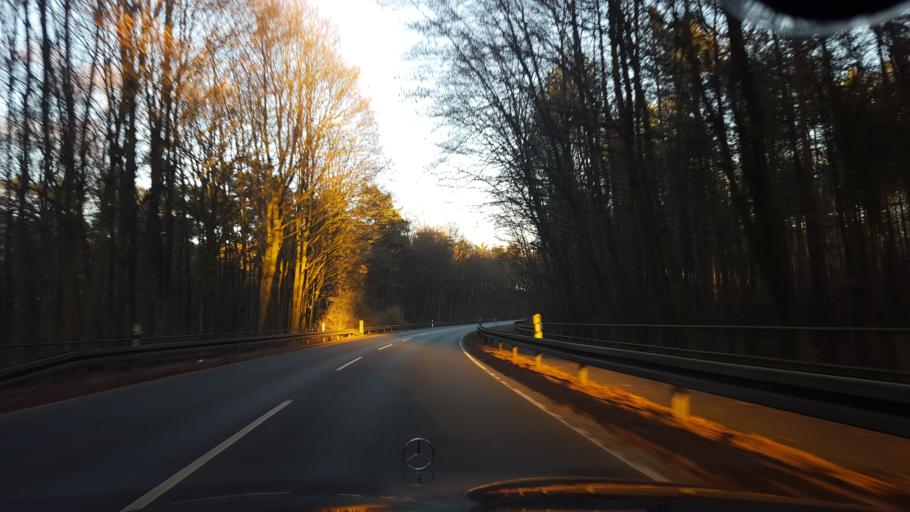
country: DE
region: North Rhine-Westphalia
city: Oer-Erkenschwick
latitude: 51.6613
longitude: 7.2614
